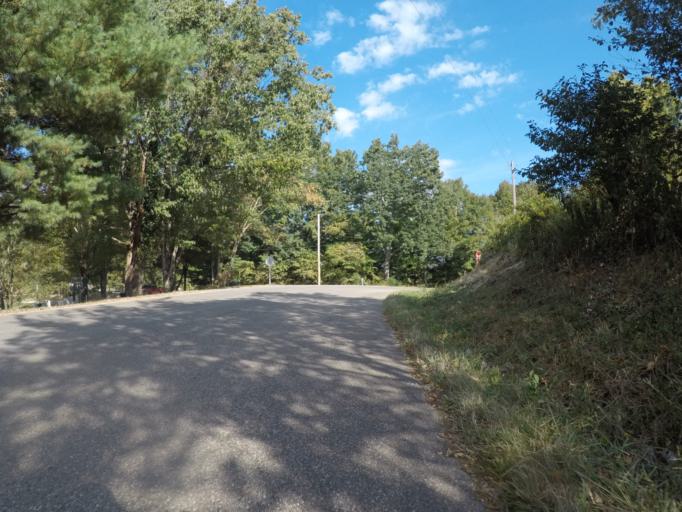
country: US
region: West Virginia
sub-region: Cabell County
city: Lesage
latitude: 38.6003
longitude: -82.4138
